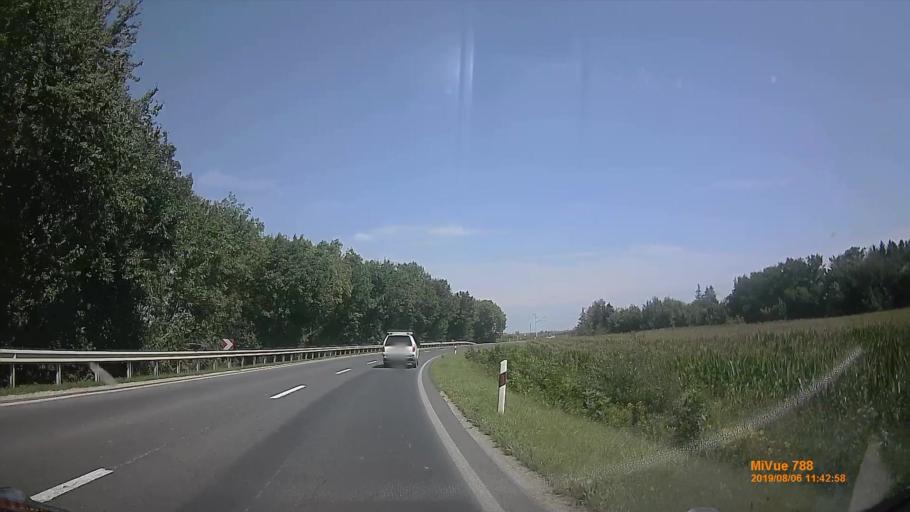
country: HU
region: Vas
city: Kormend
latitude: 47.0041
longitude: 16.5453
